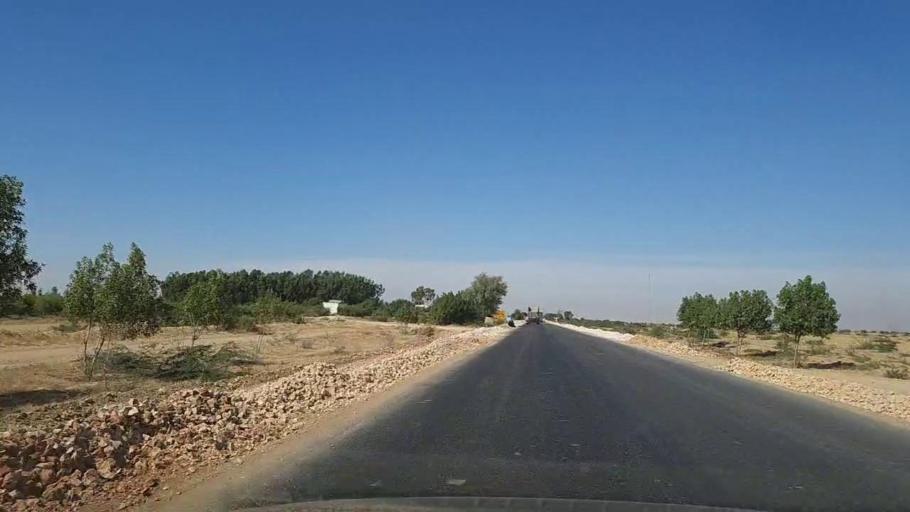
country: PK
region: Sindh
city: Kotri
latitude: 25.2623
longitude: 68.2216
